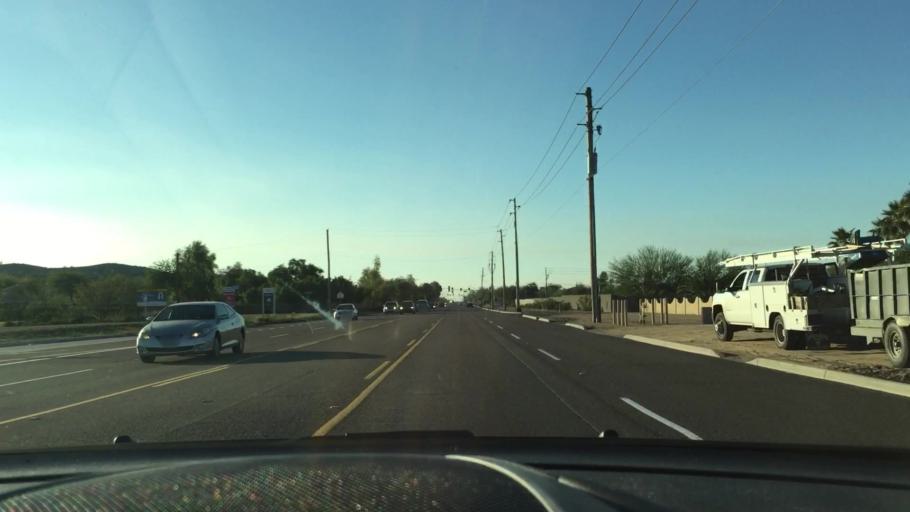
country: US
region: Arizona
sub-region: Maricopa County
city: Sun City
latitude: 33.6988
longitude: -112.2031
